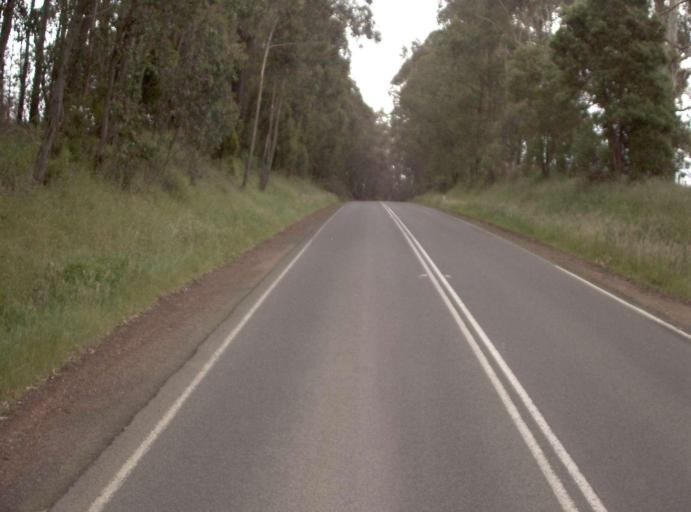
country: AU
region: Victoria
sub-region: Baw Baw
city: Warragul
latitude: -38.0776
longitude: 145.9662
